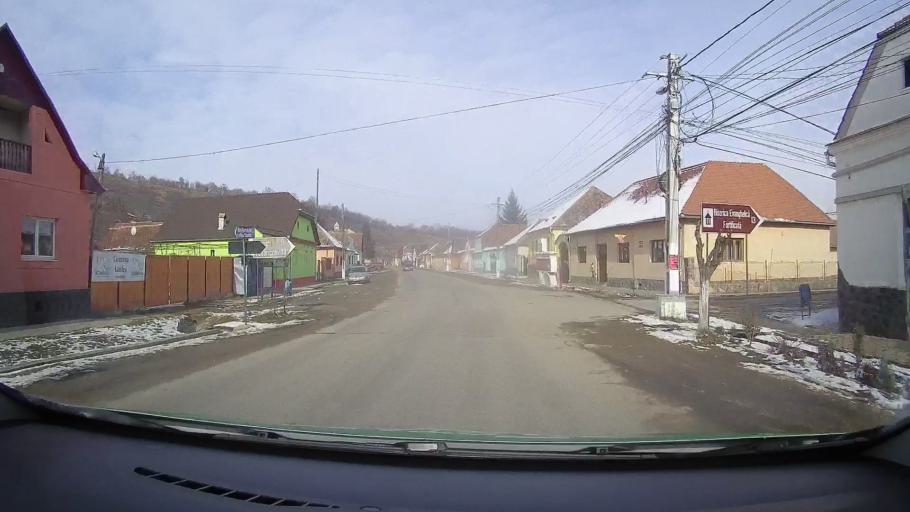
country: RO
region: Sibiu
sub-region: Comuna Laslea
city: Laslea
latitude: 46.2078
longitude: 24.6559
